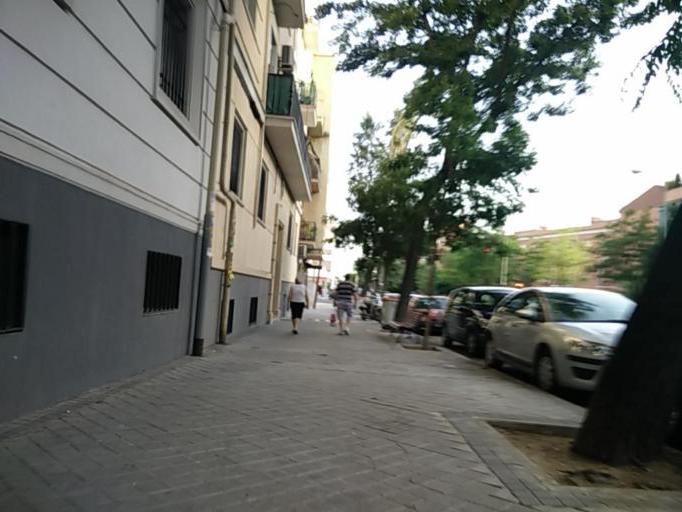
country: ES
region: Madrid
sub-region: Provincia de Madrid
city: Madrid
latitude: 40.4117
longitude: -3.7179
